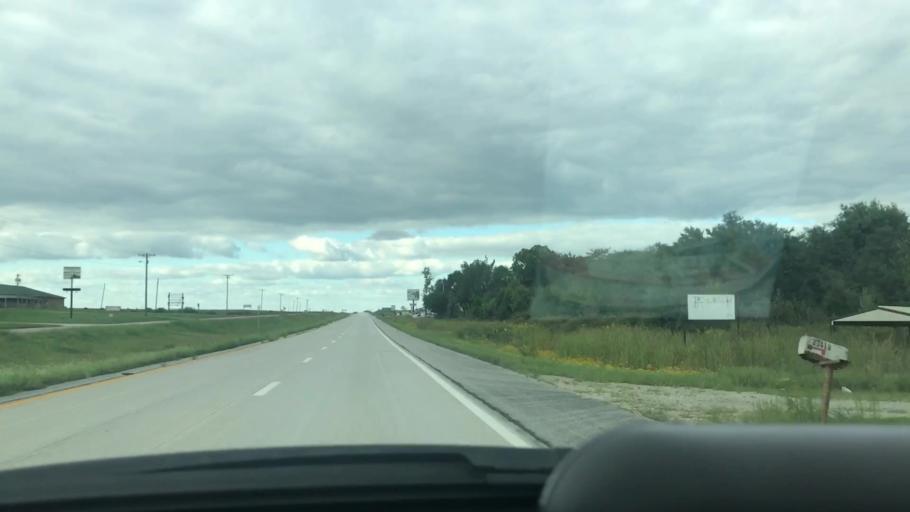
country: US
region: Missouri
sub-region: Benton County
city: Lincoln
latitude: 38.3489
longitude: -93.3399
